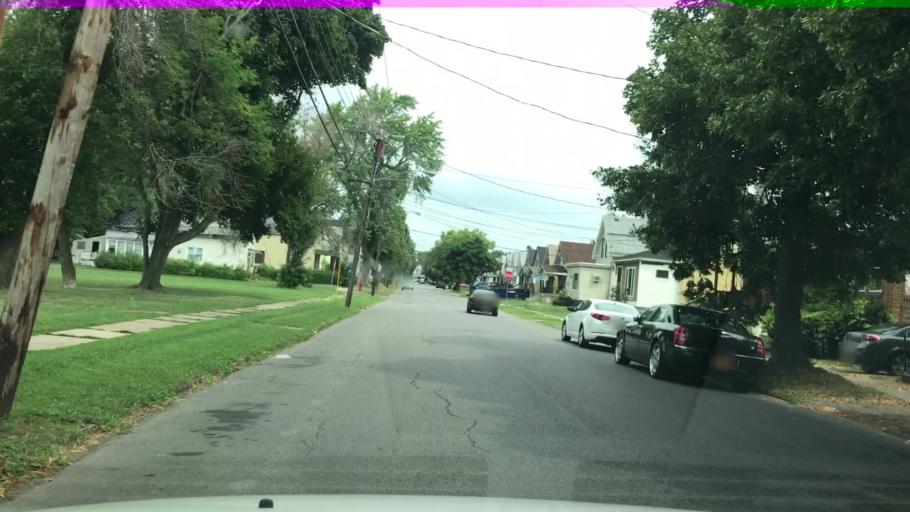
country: US
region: New York
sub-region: Erie County
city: Sloan
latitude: 42.9129
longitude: -78.8038
